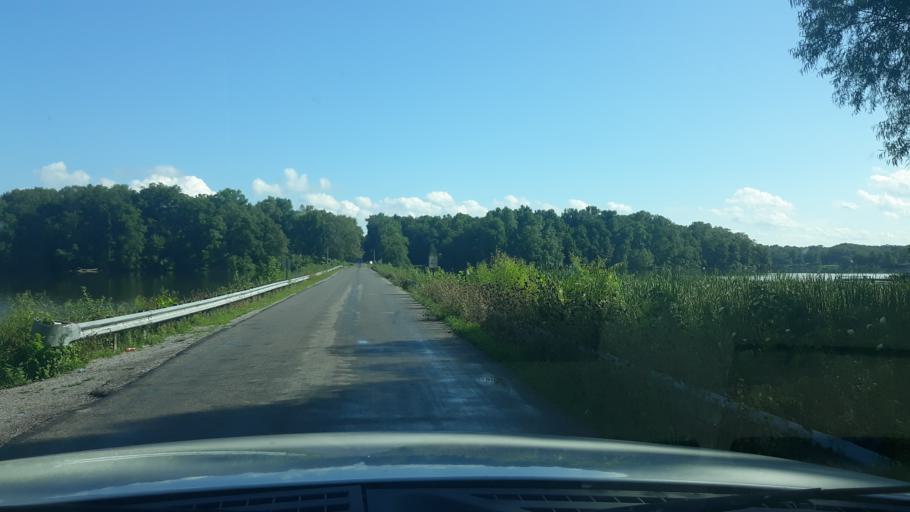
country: US
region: Illinois
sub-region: Saline County
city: Harrisburg
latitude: 37.8559
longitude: -88.5814
